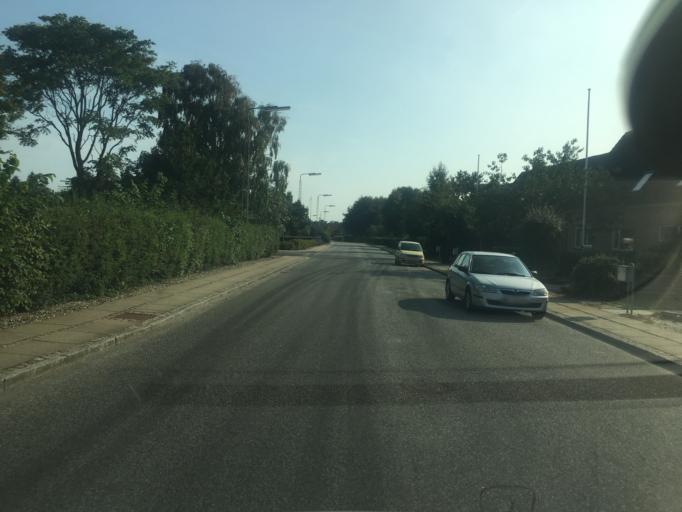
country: DK
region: South Denmark
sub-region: Tonder Kommune
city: Tonder
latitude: 54.9473
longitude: 8.8795
